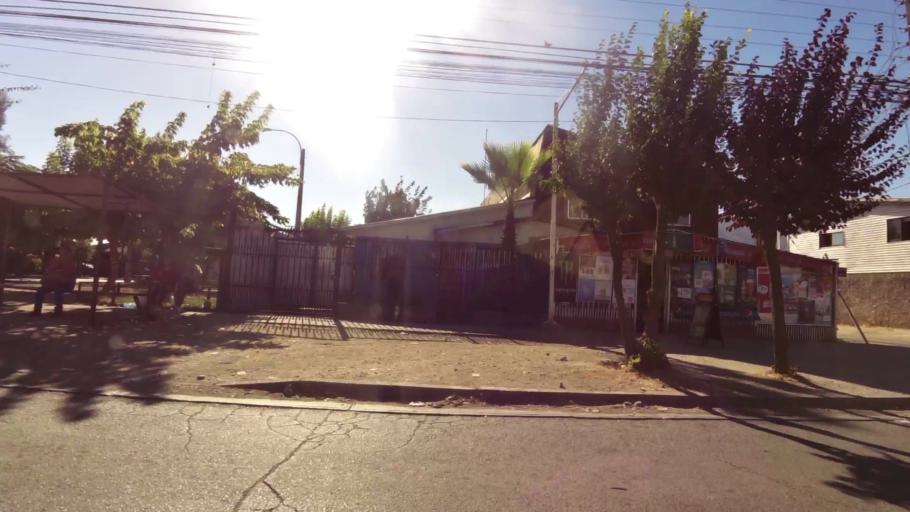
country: CL
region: O'Higgins
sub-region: Provincia de Colchagua
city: Chimbarongo
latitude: -34.5748
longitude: -70.9982
